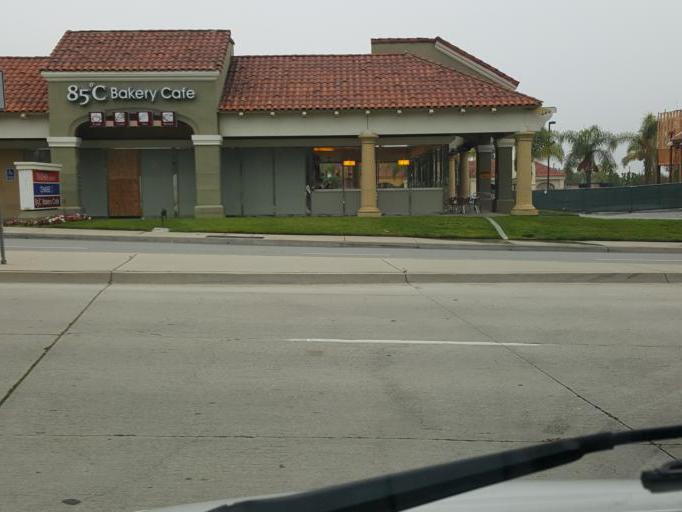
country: US
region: California
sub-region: Los Angeles County
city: Rowland Heights
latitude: 33.9900
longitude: -117.9318
